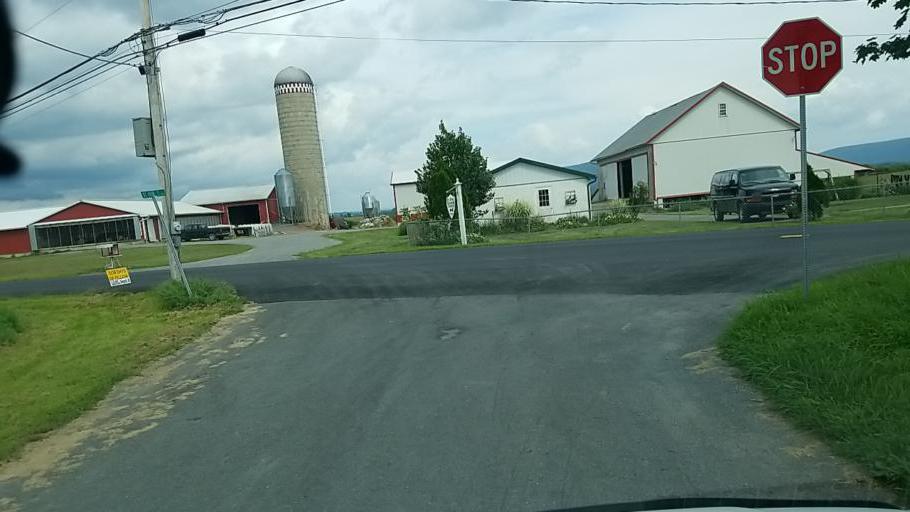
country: US
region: Pennsylvania
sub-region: Dauphin County
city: Elizabethville
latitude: 40.5881
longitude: -76.8130
